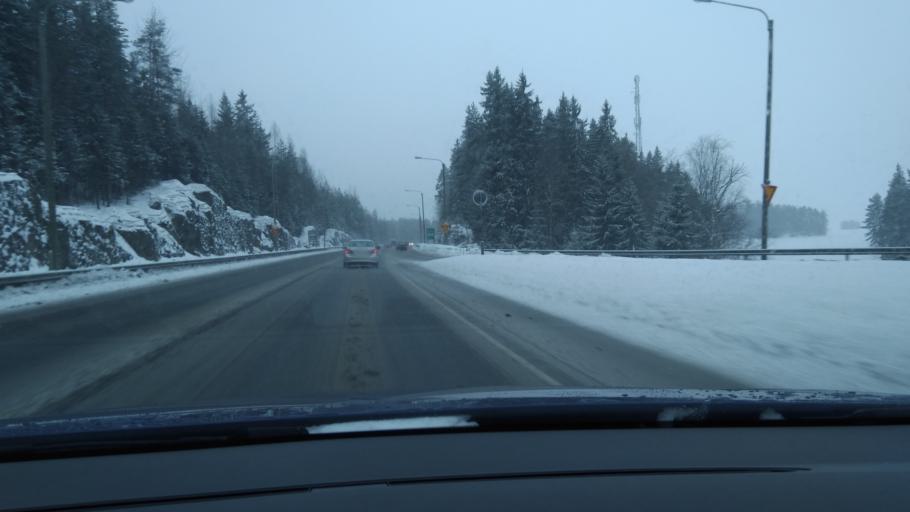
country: FI
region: Pirkanmaa
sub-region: Tampere
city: Kangasala
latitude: 61.5311
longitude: 23.9485
